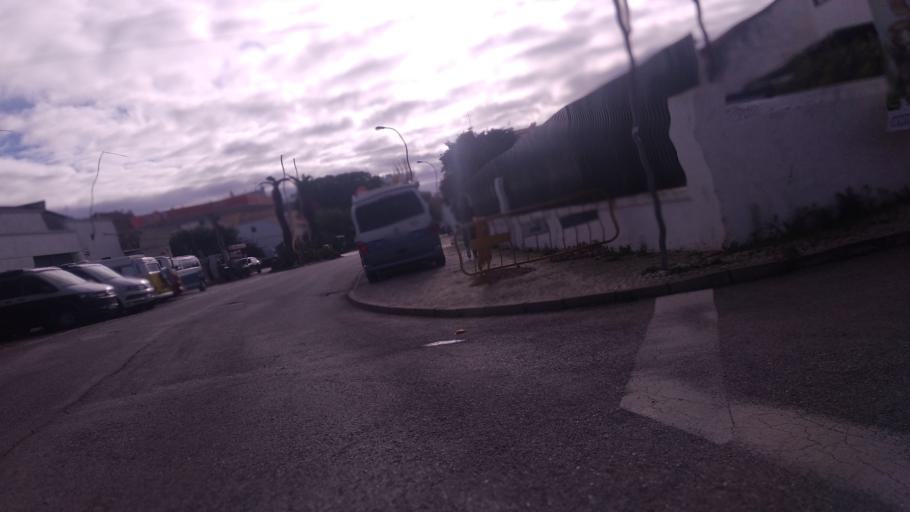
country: PT
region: Faro
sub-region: Sao Bras de Alportel
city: Sao Bras de Alportel
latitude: 37.1571
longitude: -7.8927
